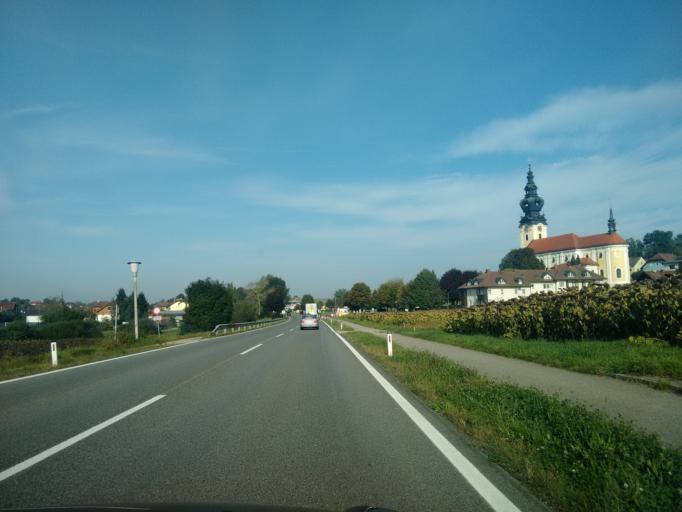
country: AT
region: Upper Austria
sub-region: Politischer Bezirk Grieskirchen
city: Grieskirchen
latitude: 48.2796
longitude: 13.7157
